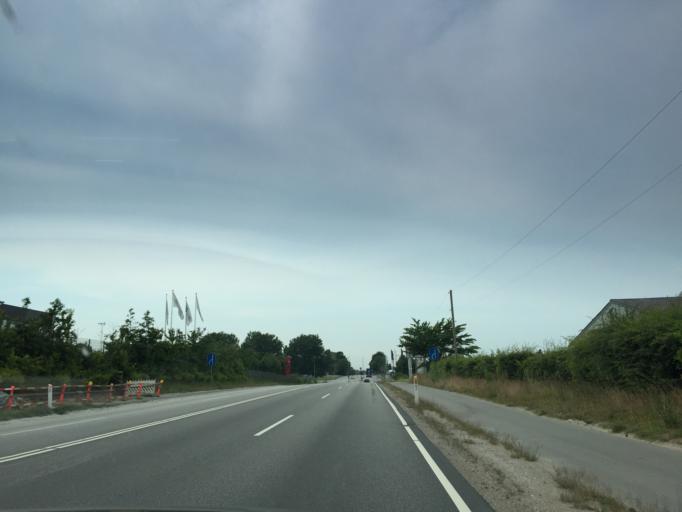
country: DK
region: Zealand
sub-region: Roskilde Kommune
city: Vindinge
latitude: 55.6453
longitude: 12.1482
